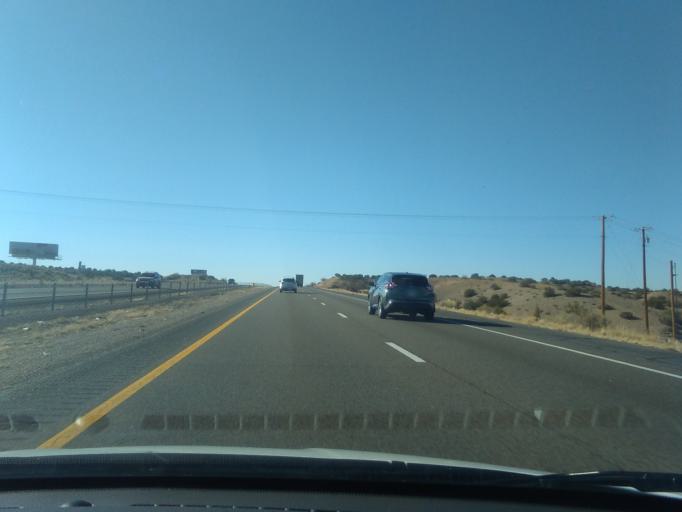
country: US
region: New Mexico
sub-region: Sandoval County
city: San Felipe Pueblo
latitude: 35.3698
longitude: -106.4805
